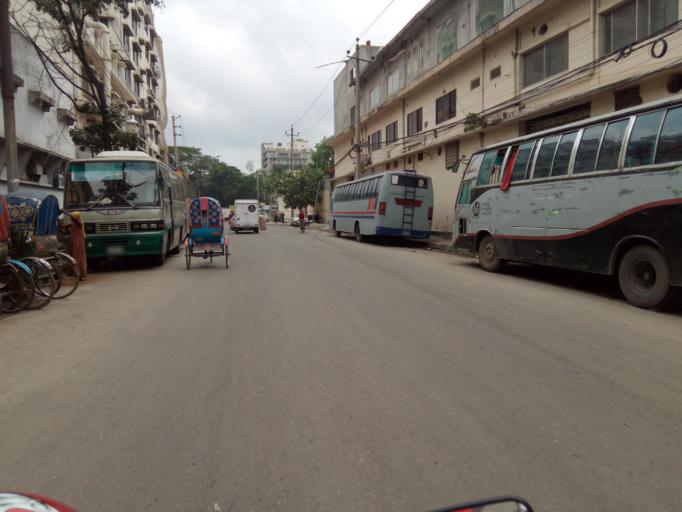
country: BD
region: Dhaka
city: Paltan
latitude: 23.7666
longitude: 90.4053
